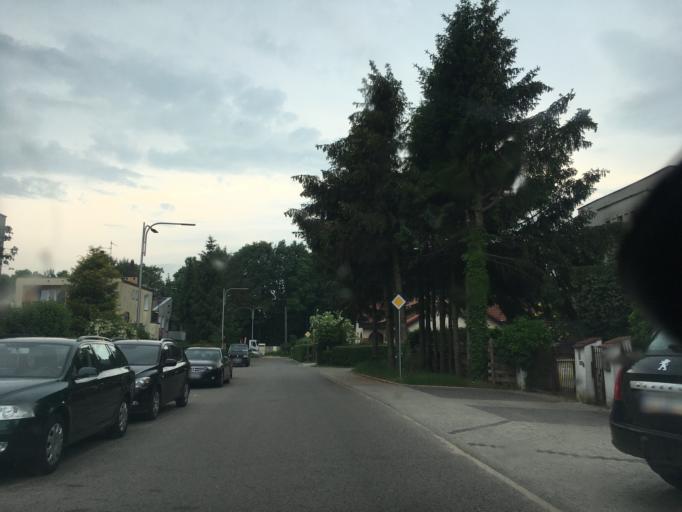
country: PL
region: West Pomeranian Voivodeship
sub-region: Koszalin
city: Koszalin
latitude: 54.1859
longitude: 16.2148
